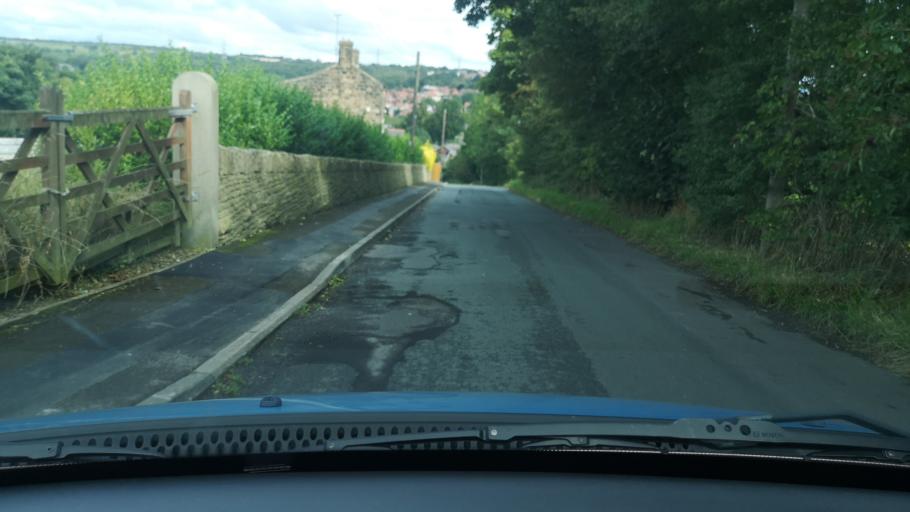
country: GB
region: England
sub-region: Kirklees
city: Heckmondwike
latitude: 53.7286
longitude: -1.6721
